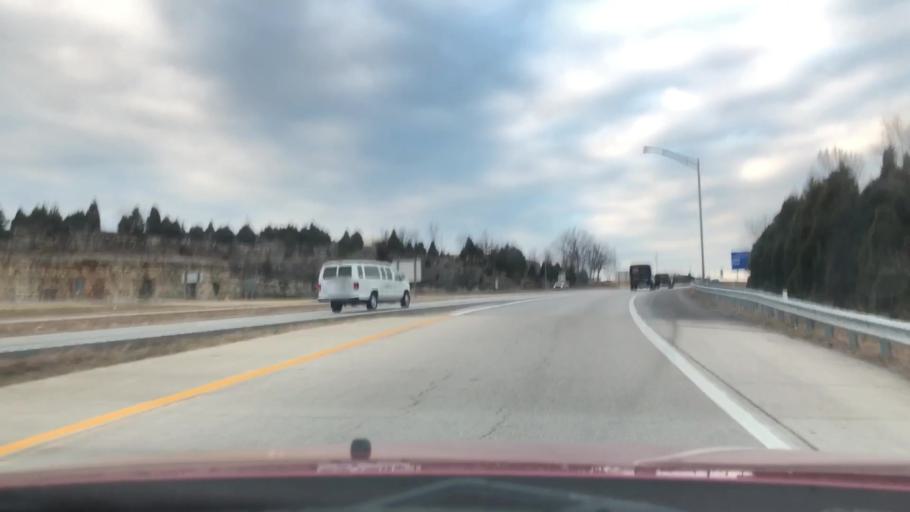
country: US
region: Missouri
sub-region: Taney County
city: Branson
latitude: 36.6587
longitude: -93.2218
